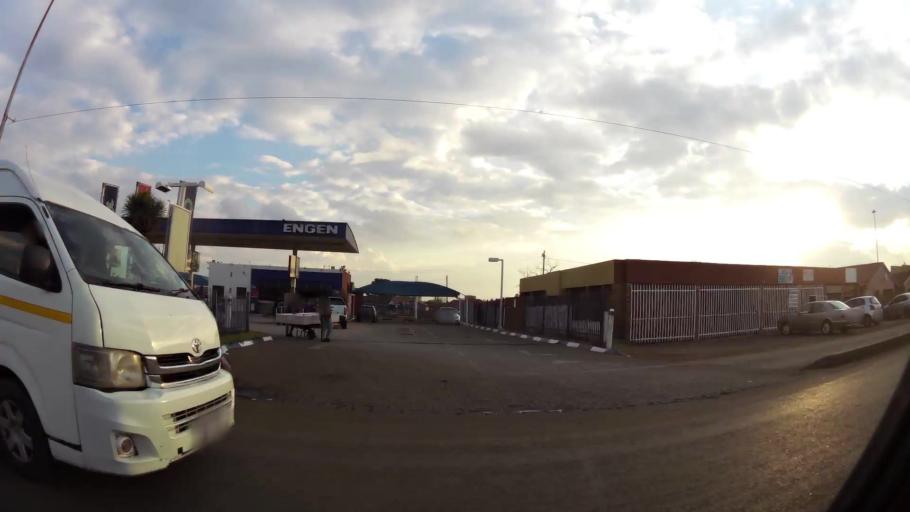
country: ZA
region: Gauteng
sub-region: City of Johannesburg Metropolitan Municipality
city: Orange Farm
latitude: -26.5878
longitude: 27.8461
